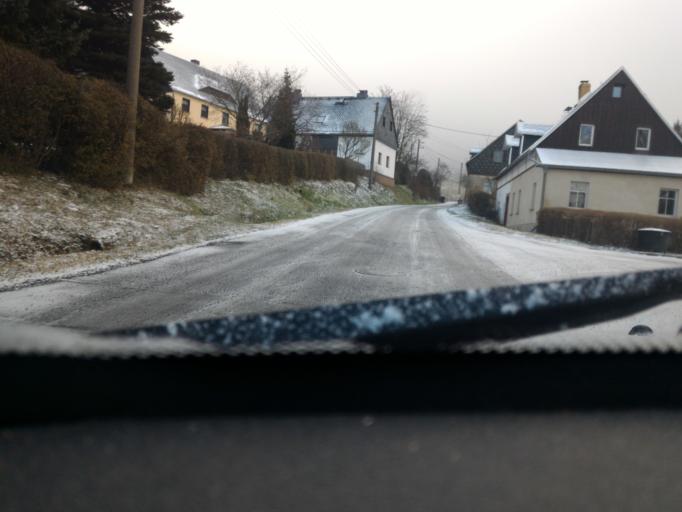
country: DE
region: Saxony
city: Grossschonau
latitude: 50.8619
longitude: 14.6513
